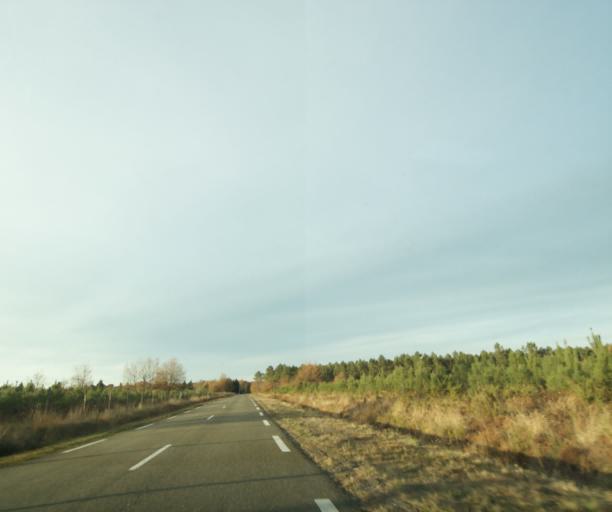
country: FR
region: Aquitaine
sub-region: Departement des Landes
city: Gabarret
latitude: 44.1507
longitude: -0.1278
